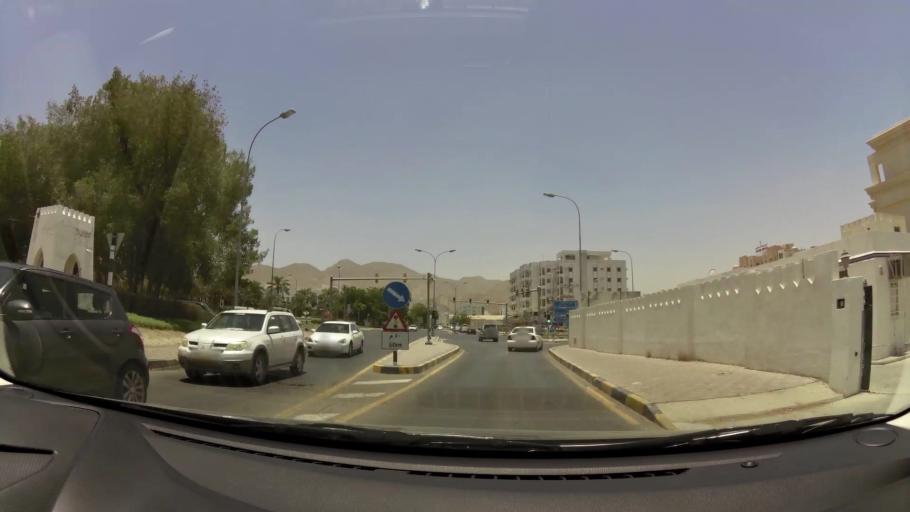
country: OM
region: Muhafazat Masqat
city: Bawshar
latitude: 23.5978
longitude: 58.4495
